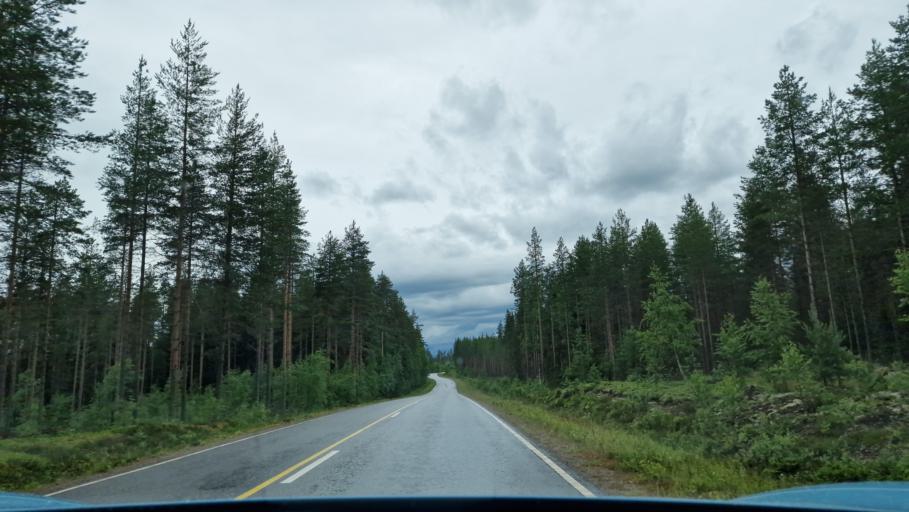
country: FI
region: Central Finland
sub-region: Saarijaervi-Viitasaari
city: Pylkoenmaeki
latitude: 62.6690
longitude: 24.5276
